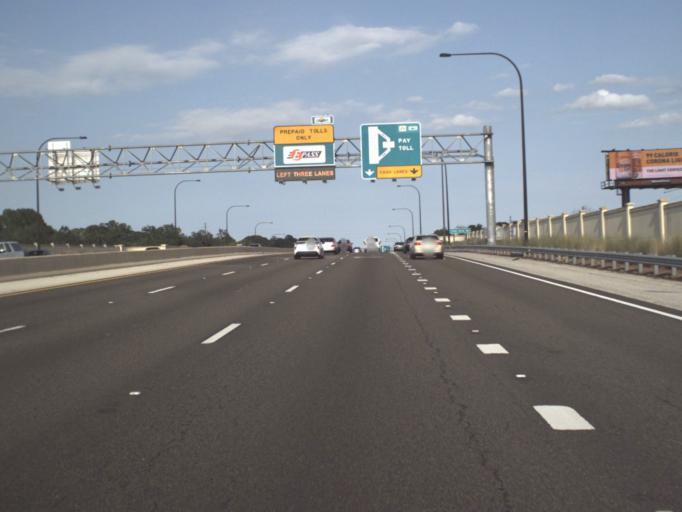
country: US
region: Florida
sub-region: Orange County
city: Pine Hills
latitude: 28.5482
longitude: -81.4495
